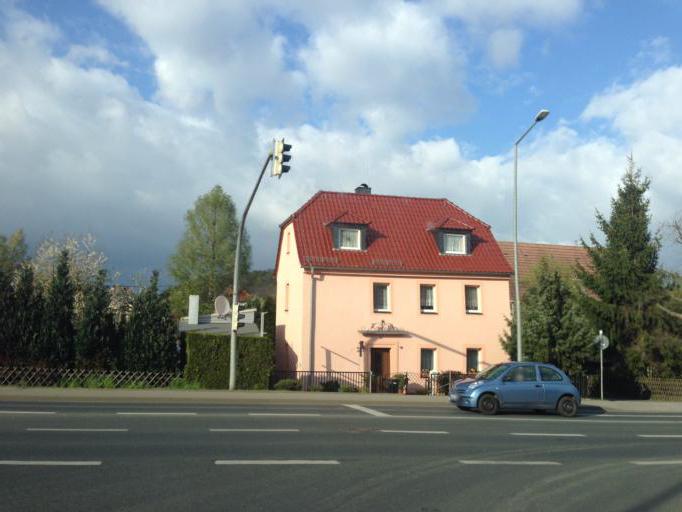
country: DE
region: Saxony
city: Freital
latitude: 51.0151
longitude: 13.6429
